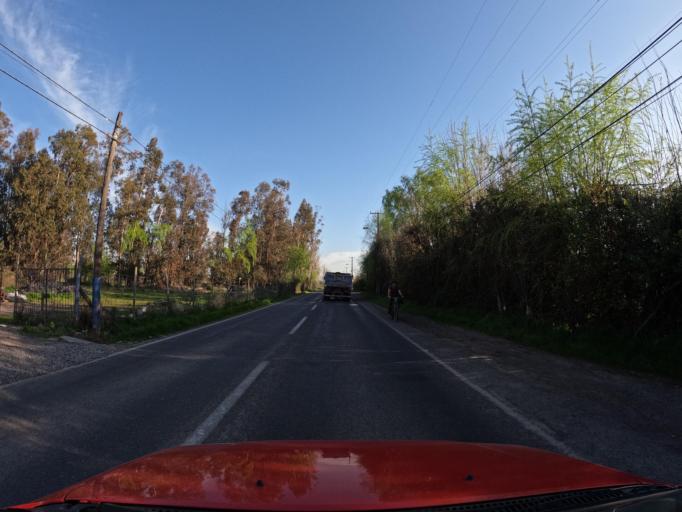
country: CL
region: Maule
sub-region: Provincia de Curico
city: Rauco
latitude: -34.8818
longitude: -71.2704
